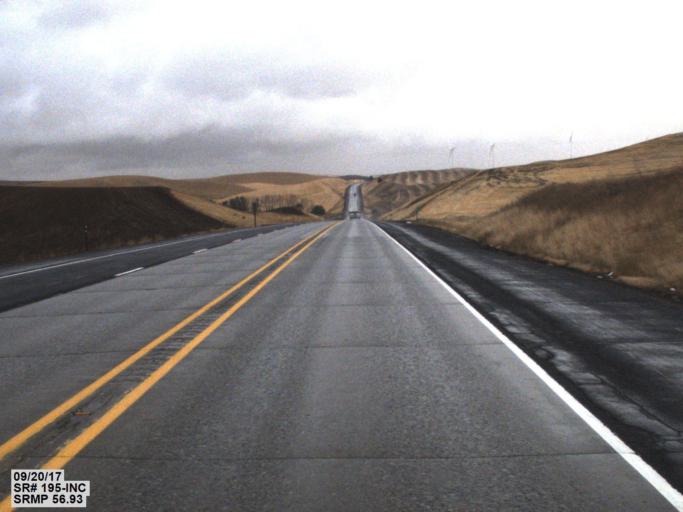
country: US
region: Washington
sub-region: Whitman County
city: Colfax
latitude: 47.1304
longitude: -117.3793
